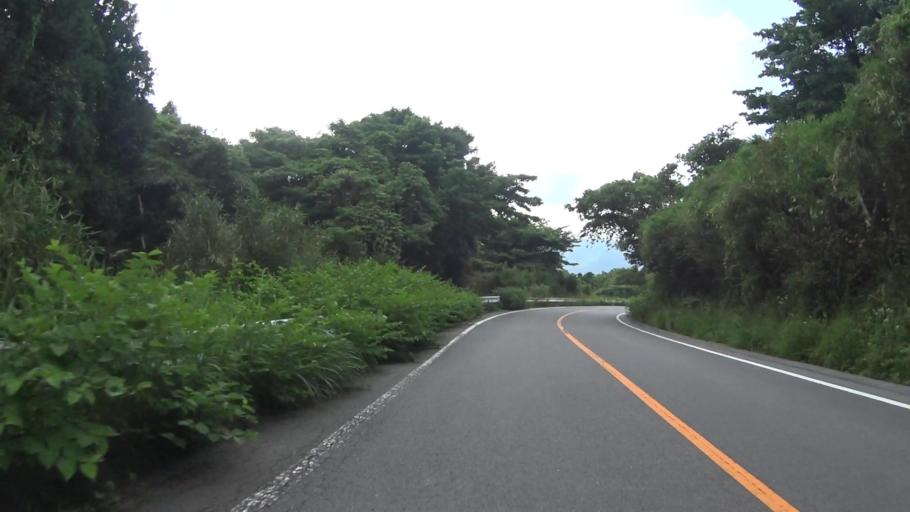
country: JP
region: Kumamoto
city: Aso
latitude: 32.8951
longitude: 131.0184
